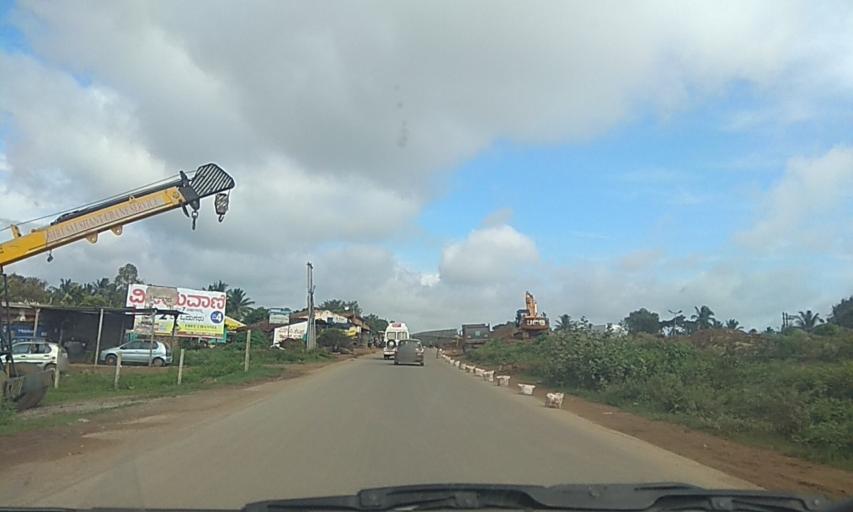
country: IN
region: Karnataka
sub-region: Haveri
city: Shiggaon
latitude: 14.9904
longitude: 75.2179
